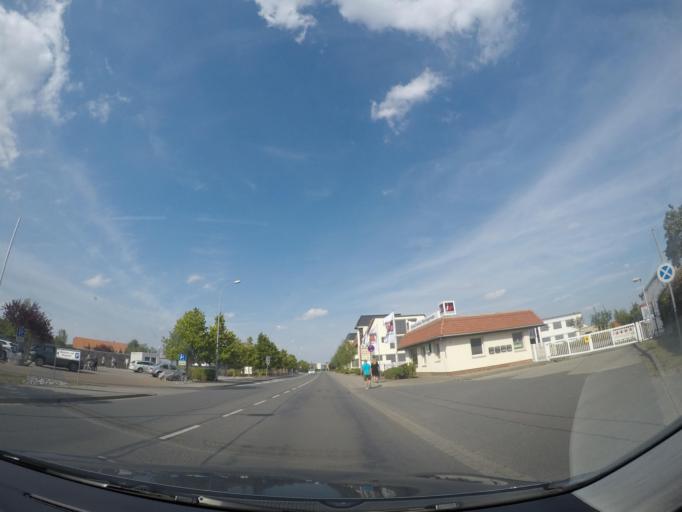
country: DE
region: Saxony-Anhalt
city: Wernigerode
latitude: 51.8441
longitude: 10.7828
